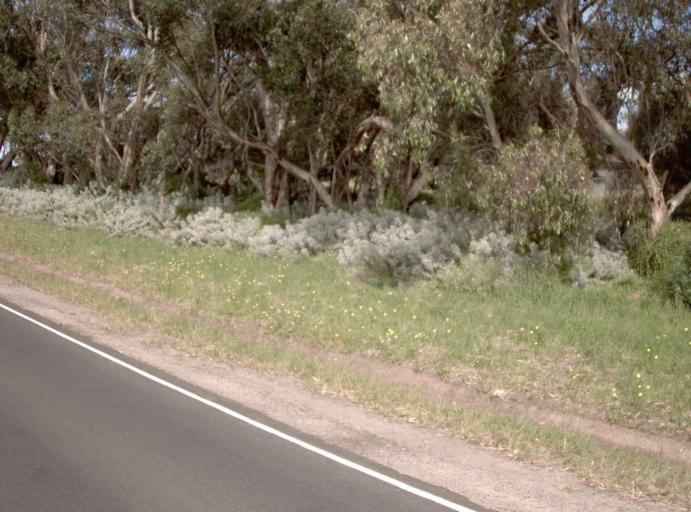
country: AU
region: Victoria
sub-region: Bass Coast
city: Phillip Island
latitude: -38.4695
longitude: 145.1906
